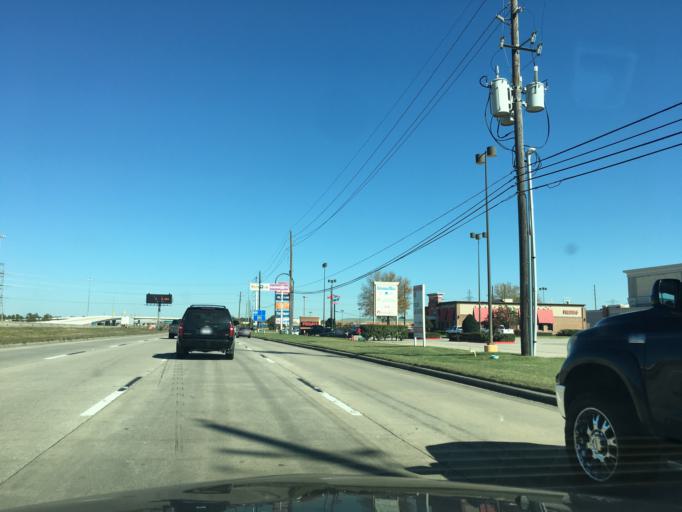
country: US
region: Texas
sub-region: Harris County
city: Humble
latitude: 30.0124
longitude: -95.2638
